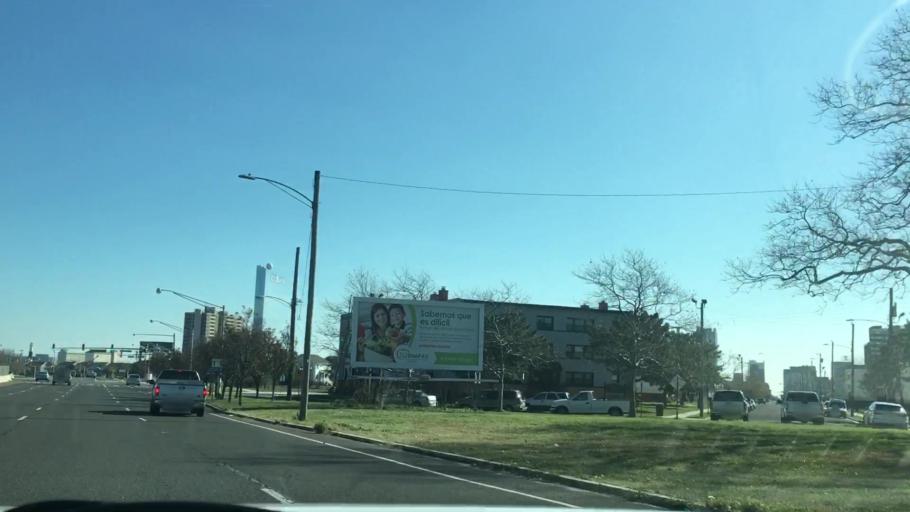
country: US
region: New Jersey
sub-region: Atlantic County
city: Atlantic City
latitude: 39.3712
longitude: -74.4325
